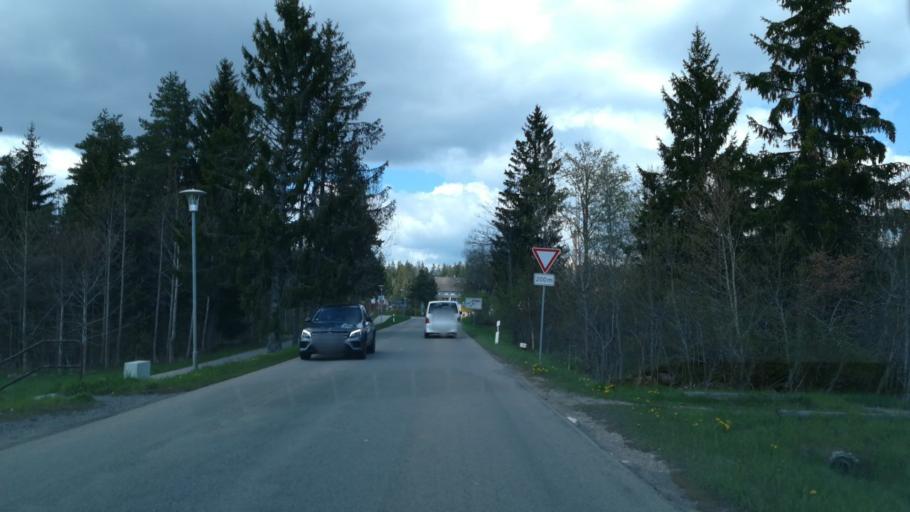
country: DE
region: Baden-Wuerttemberg
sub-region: Freiburg Region
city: Grafenhausen
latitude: 47.7926
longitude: 8.2463
